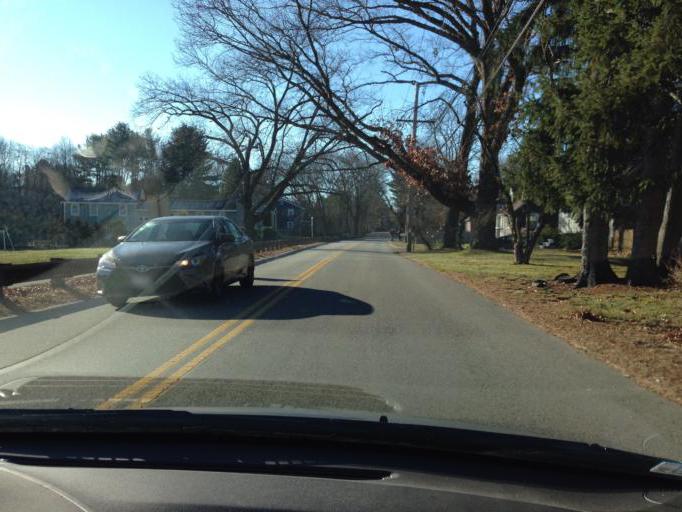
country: US
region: Massachusetts
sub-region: Middlesex County
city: Bedford
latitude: 42.4997
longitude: -71.2729
